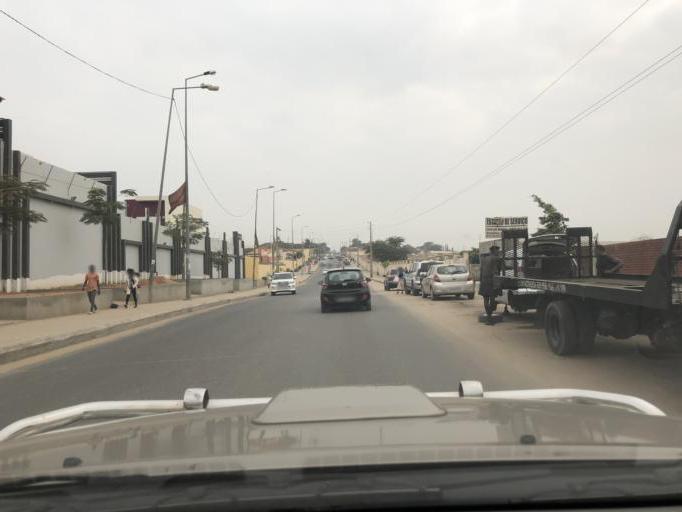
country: AO
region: Luanda
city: Luanda
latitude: -8.9045
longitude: 13.2159
